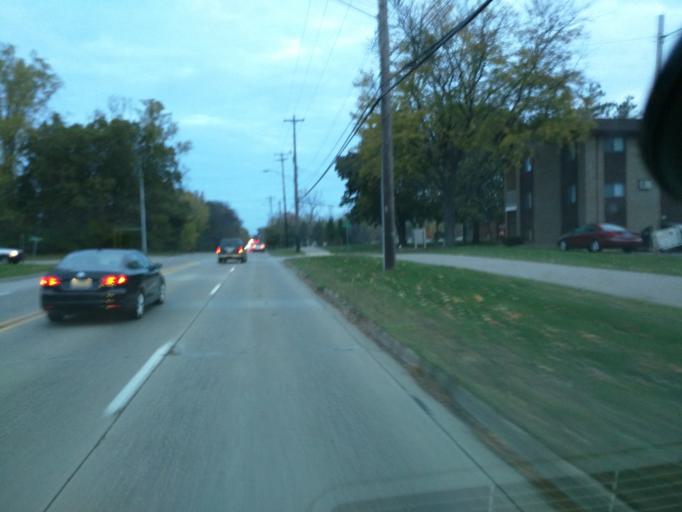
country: US
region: Michigan
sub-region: Eaton County
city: Waverly
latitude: 42.7031
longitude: -84.6031
